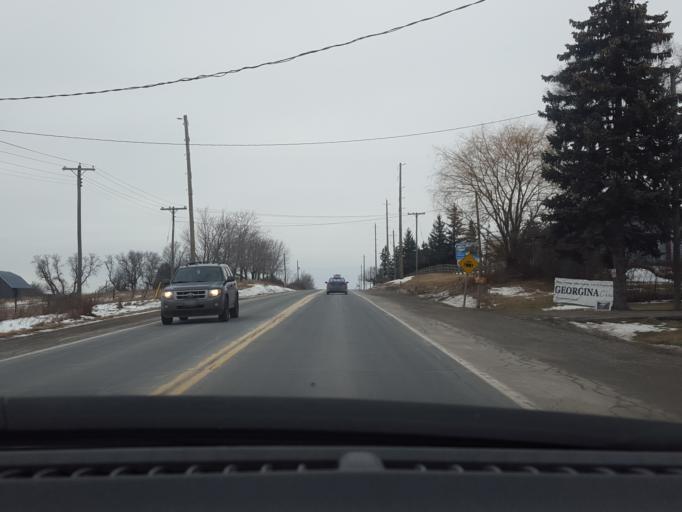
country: CA
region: Ontario
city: Newmarket
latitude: 44.1480
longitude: -79.4269
